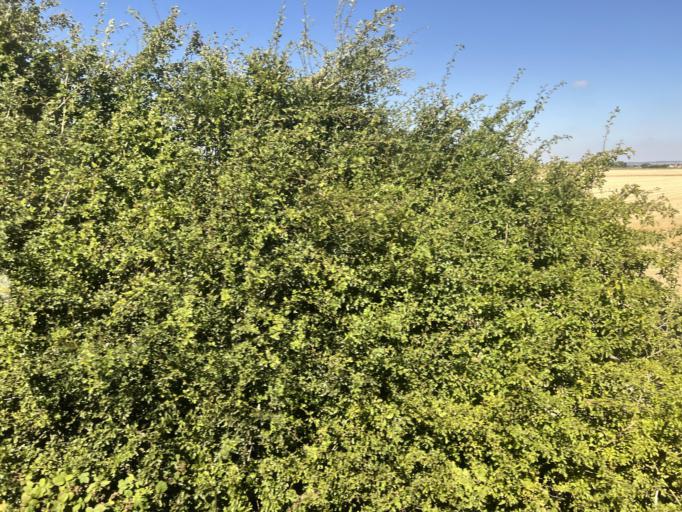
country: GB
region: England
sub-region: Lincolnshire
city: Spilsby
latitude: 53.0652
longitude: 0.0652
